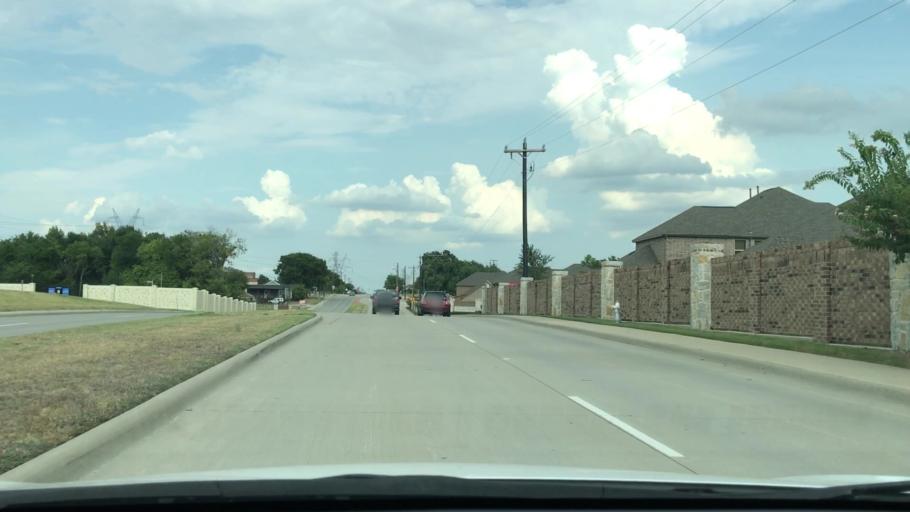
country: US
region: Texas
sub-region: Collin County
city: Wylie
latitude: 33.0168
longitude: -96.5226
